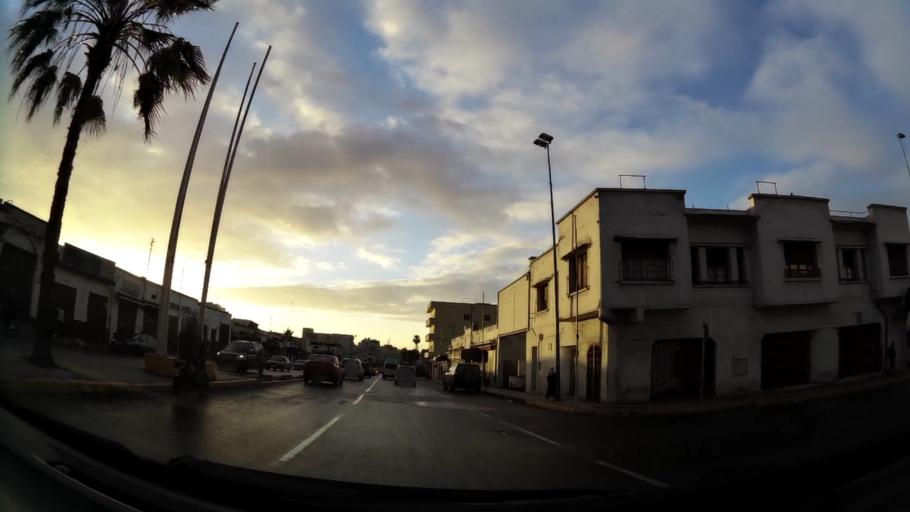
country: MA
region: Grand Casablanca
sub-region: Casablanca
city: Casablanca
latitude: 33.5822
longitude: -7.6027
